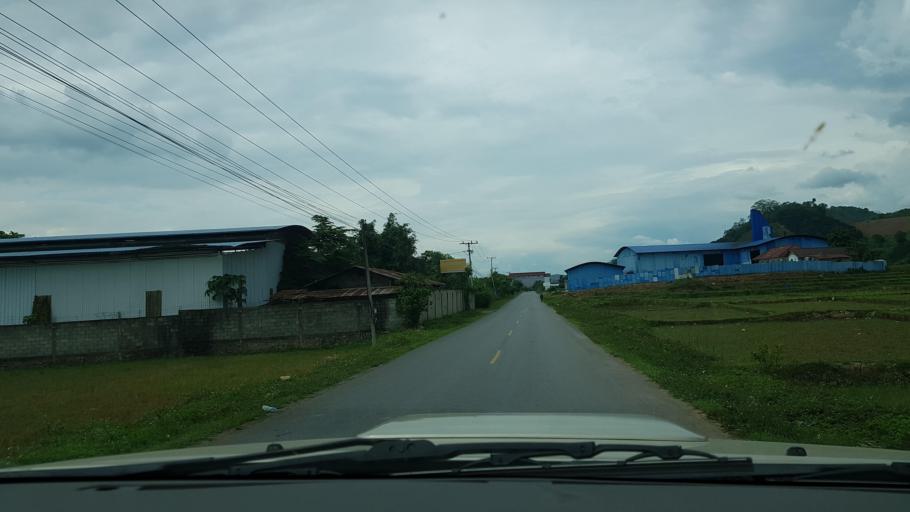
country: LA
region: Loungnamtha
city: Muang Nale
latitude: 20.3333
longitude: 101.6713
